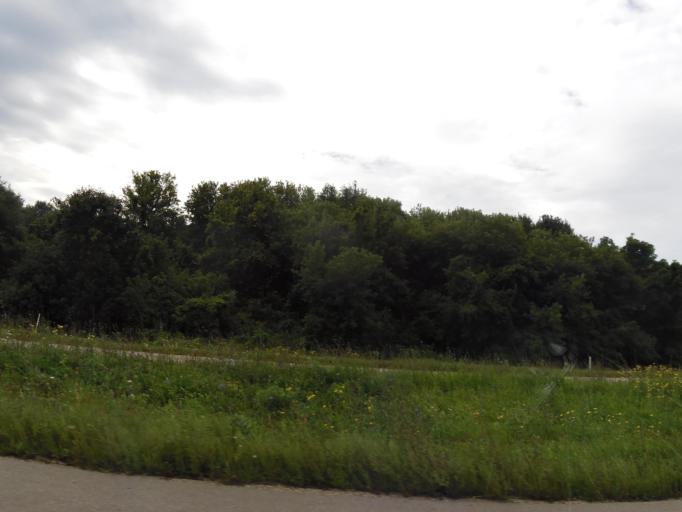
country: US
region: Wisconsin
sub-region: La Crosse County
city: West Salem
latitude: 43.8918
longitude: -91.0724
